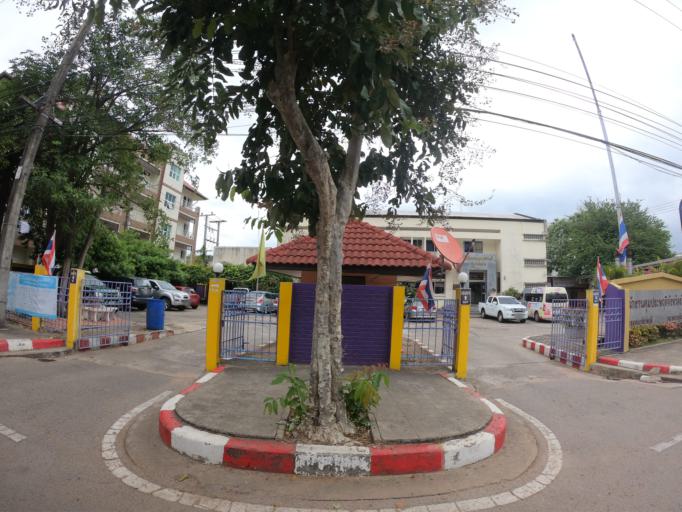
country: TH
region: Roi Et
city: Roi Et
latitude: 16.0507
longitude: 103.6538
